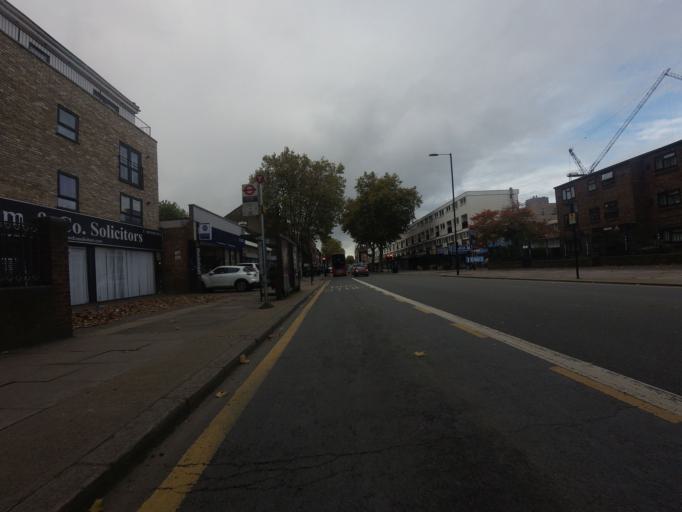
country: GB
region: England
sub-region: Greater London
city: East Ham
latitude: 51.5308
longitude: 0.0414
